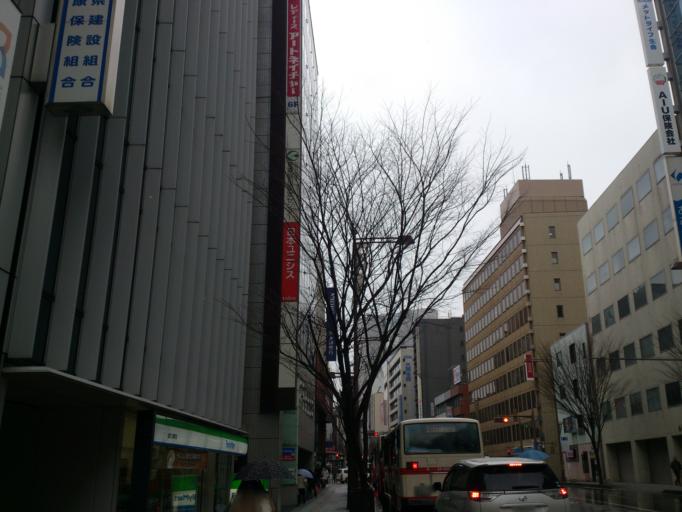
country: JP
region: Ishikawa
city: Kanazawa-shi
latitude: 36.5686
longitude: 136.6543
